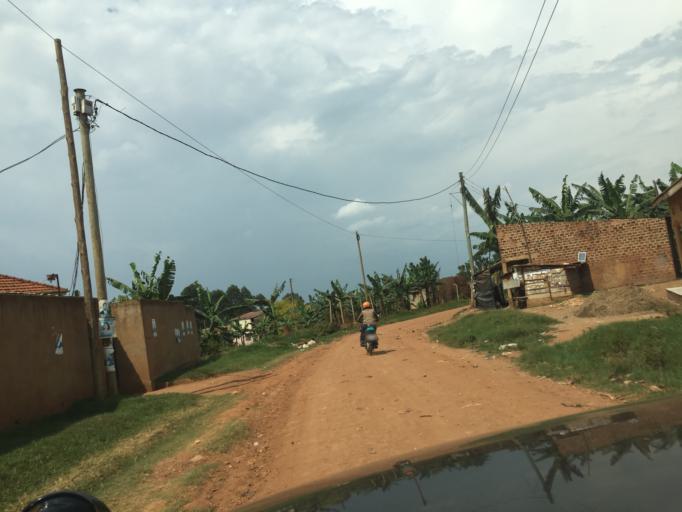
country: UG
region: Central Region
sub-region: Wakiso District
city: Kireka
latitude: 0.4132
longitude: 32.6213
